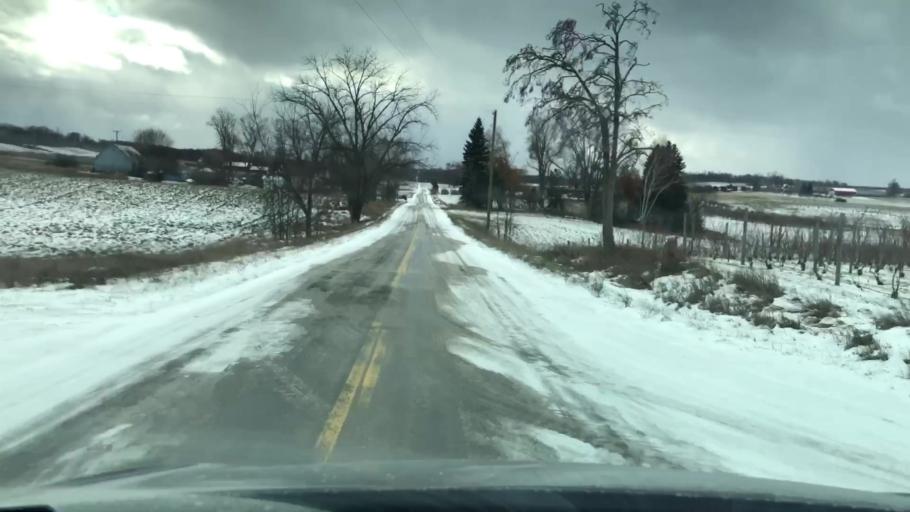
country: US
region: Michigan
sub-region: Antrim County
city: Elk Rapids
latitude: 44.9281
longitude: -85.5156
